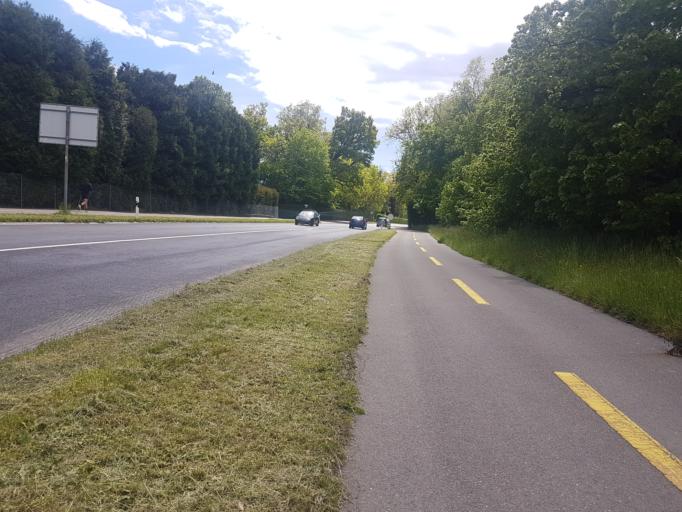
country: CH
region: Vaud
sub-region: Nyon District
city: Founex
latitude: 46.3411
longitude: 6.2049
